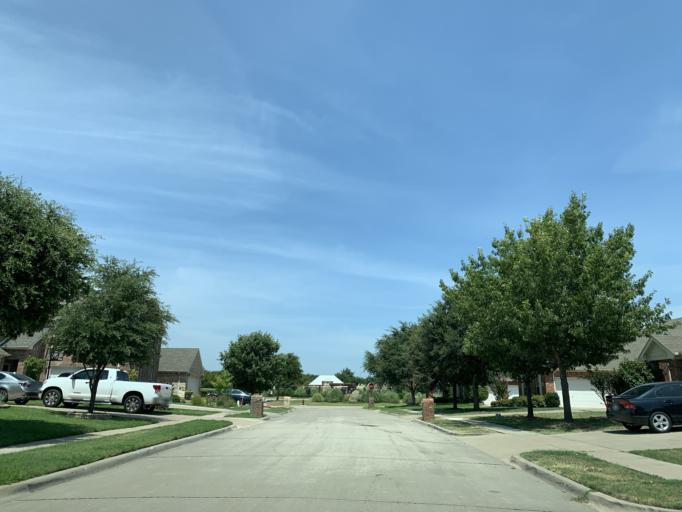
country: US
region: Texas
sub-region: Dallas County
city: Cedar Hill
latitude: 32.6447
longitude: -97.0424
